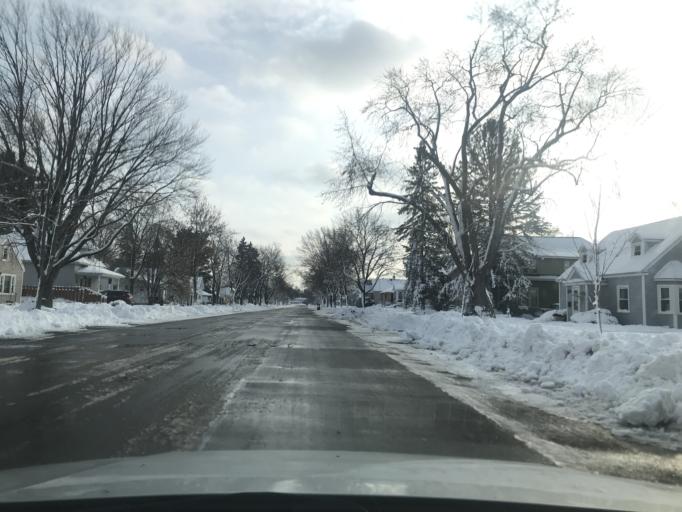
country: US
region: Wisconsin
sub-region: Marinette County
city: Peshtigo
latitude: 45.0508
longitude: -87.7550
